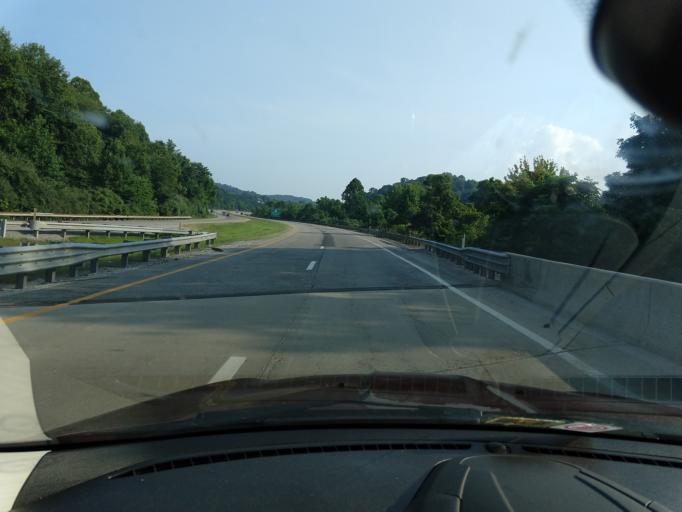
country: US
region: West Virginia
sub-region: Kanawha County
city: Sissonville
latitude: 38.4778
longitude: -81.6431
